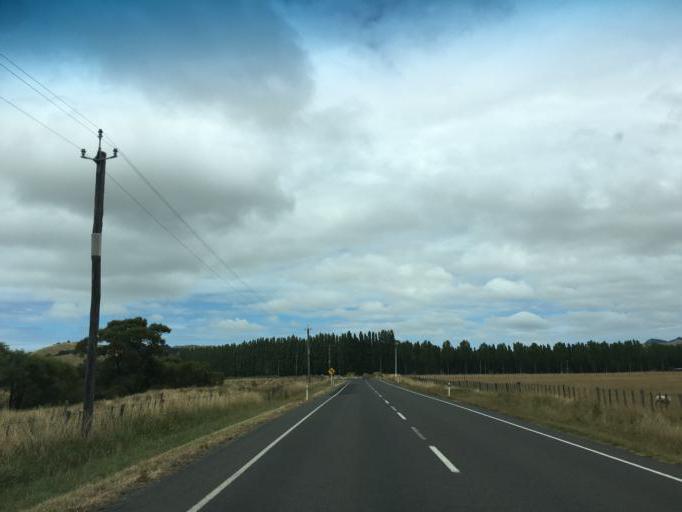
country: NZ
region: Gisborne
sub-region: Gisborne District
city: Gisborne
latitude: -38.5770
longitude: 178.1831
